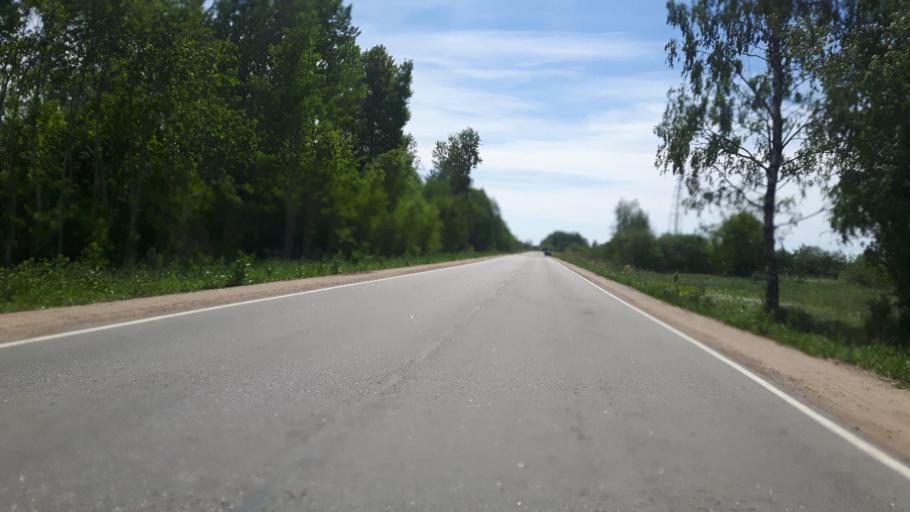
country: RU
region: Leningrad
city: Ust'-Luga
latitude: 59.5763
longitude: 28.1746
